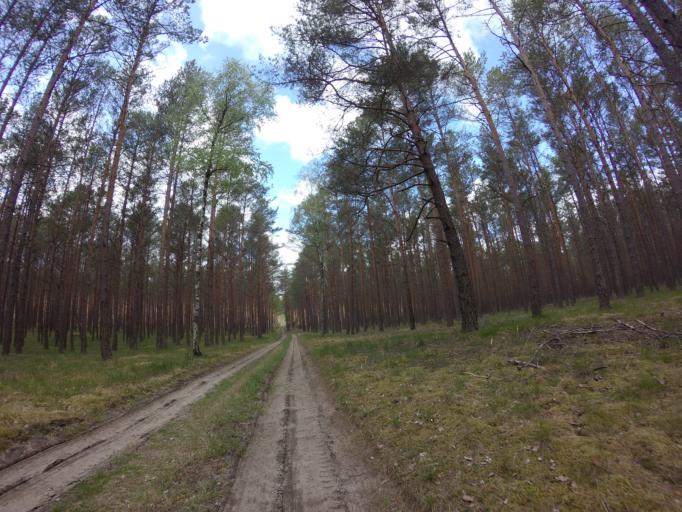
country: PL
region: West Pomeranian Voivodeship
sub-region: Powiat drawski
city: Kalisz Pomorski
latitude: 53.1941
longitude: 15.9952
